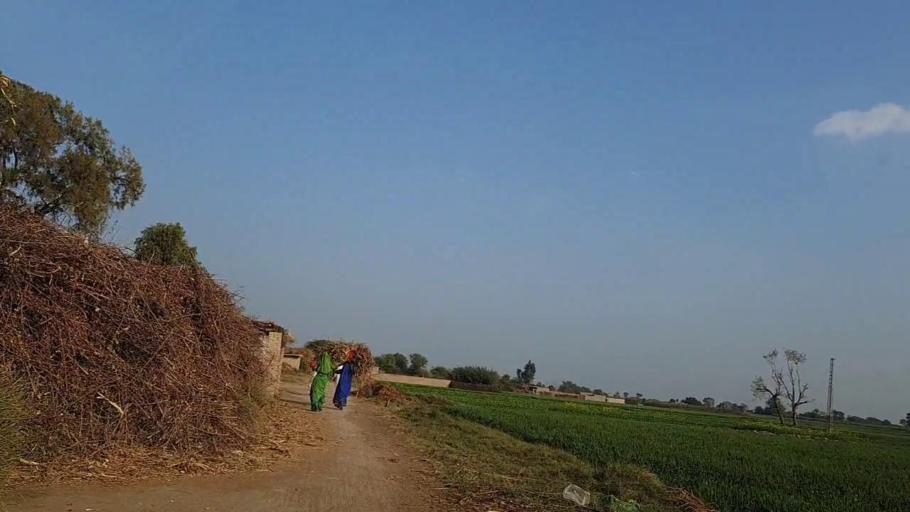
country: PK
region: Sindh
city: Nawabshah
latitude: 26.1385
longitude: 68.3870
